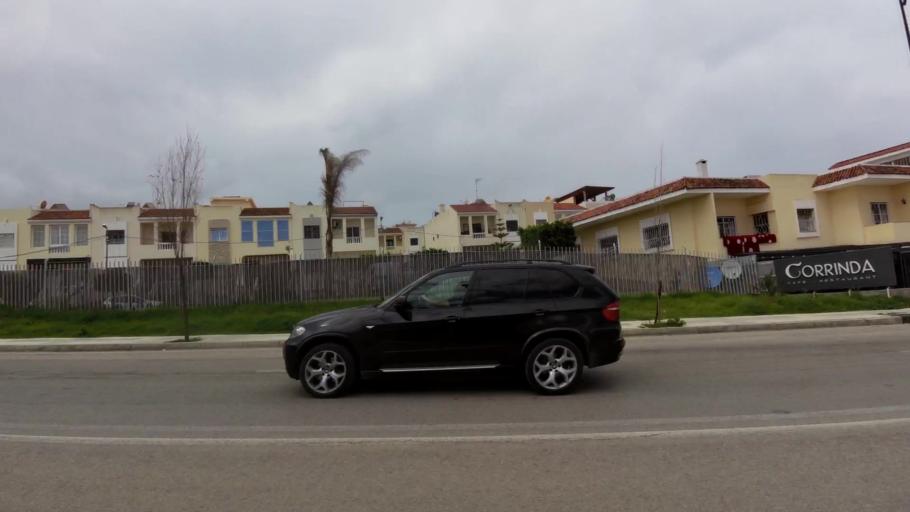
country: MA
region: Tanger-Tetouan
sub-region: Tanger-Assilah
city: Boukhalef
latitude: 35.7714
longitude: -5.8589
